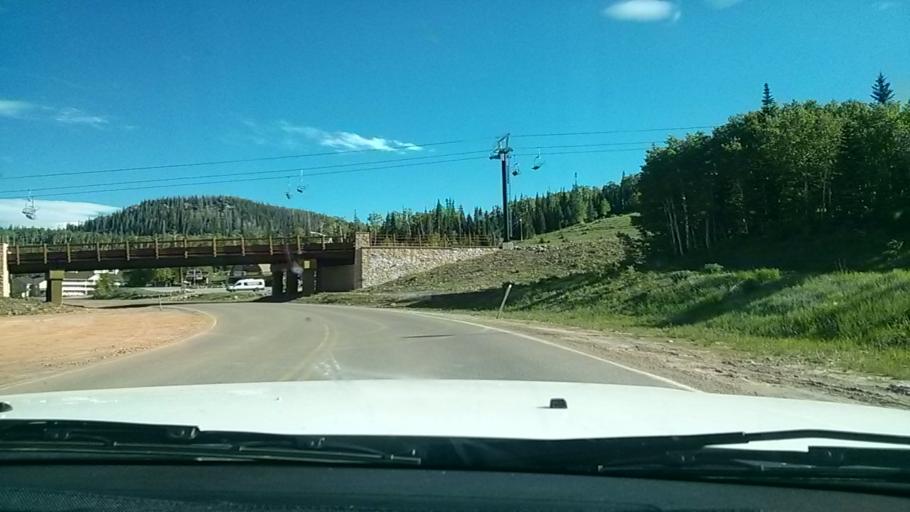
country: US
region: Utah
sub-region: Iron County
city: Parowan
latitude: 37.6895
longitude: -112.8538
